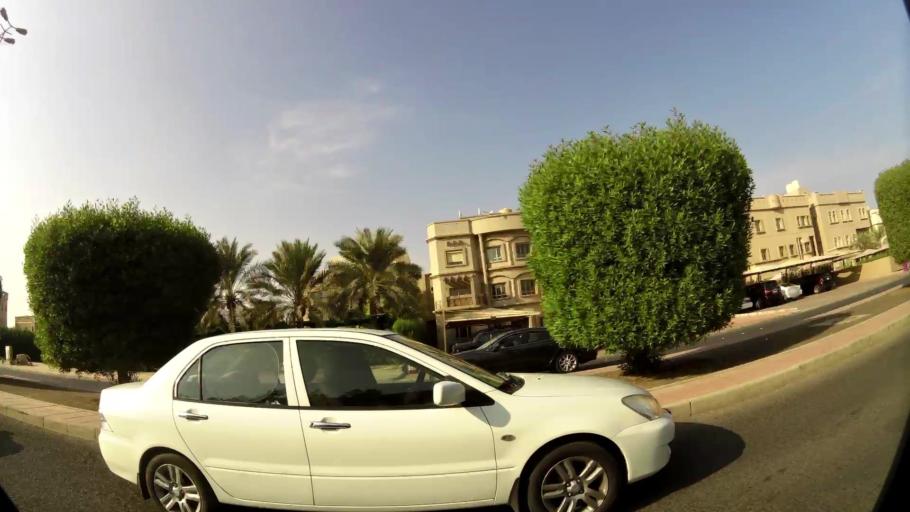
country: KW
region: Al Ahmadi
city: Al Fintas
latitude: 29.1780
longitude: 48.1090
